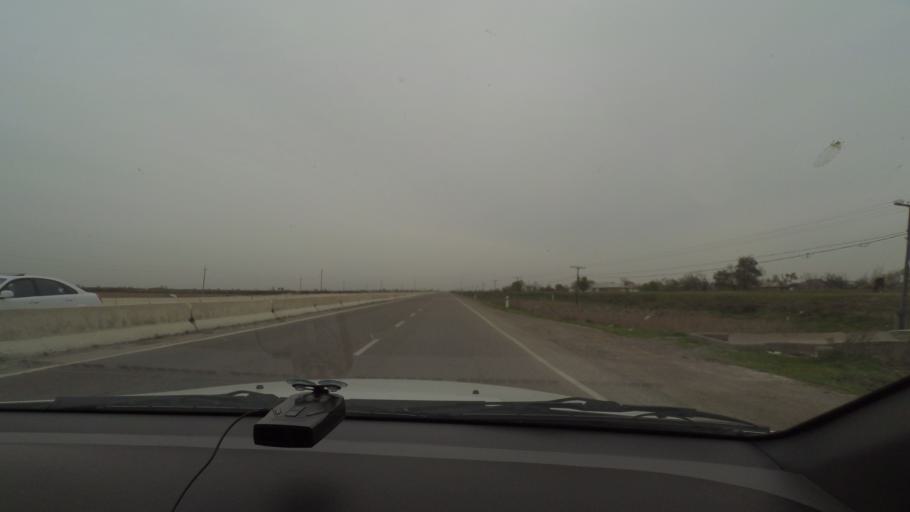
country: UZ
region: Sirdaryo
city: Guliston
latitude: 40.4945
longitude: 68.6516
